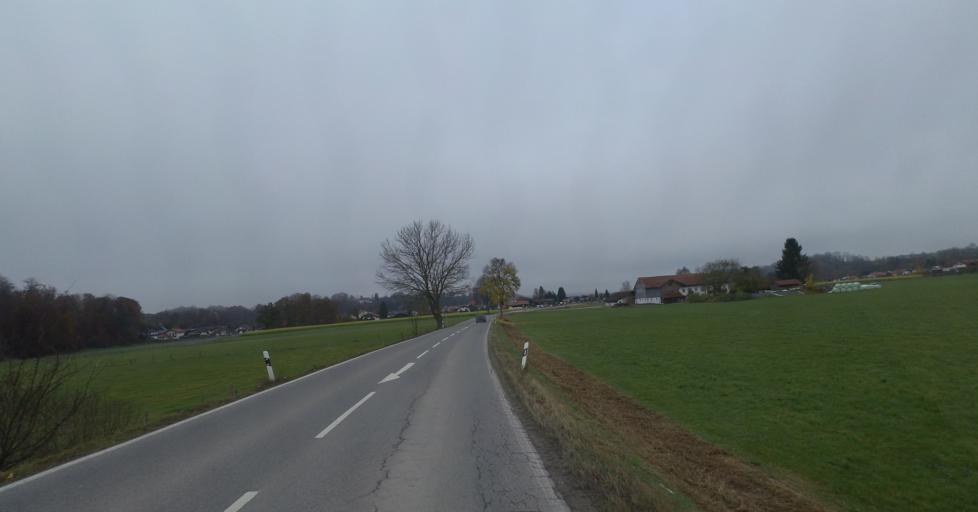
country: DE
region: Bavaria
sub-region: Upper Bavaria
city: Trostberg an der Alz
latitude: 47.9872
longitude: 12.5363
